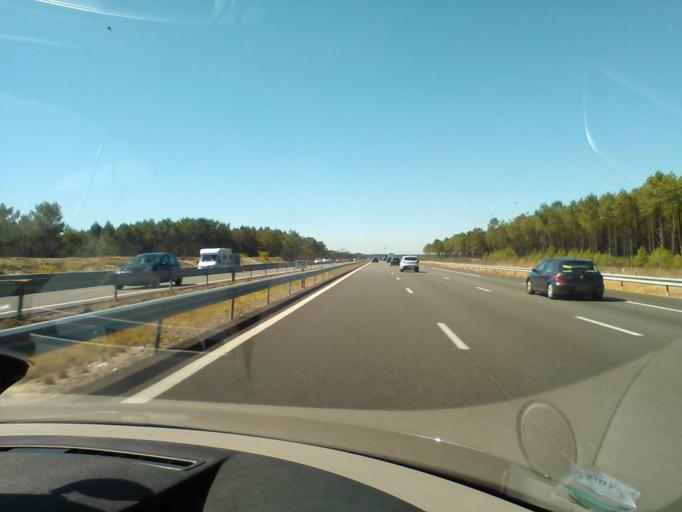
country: FR
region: Aquitaine
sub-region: Departement des Landes
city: Castets
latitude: 43.9175
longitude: -1.1171
